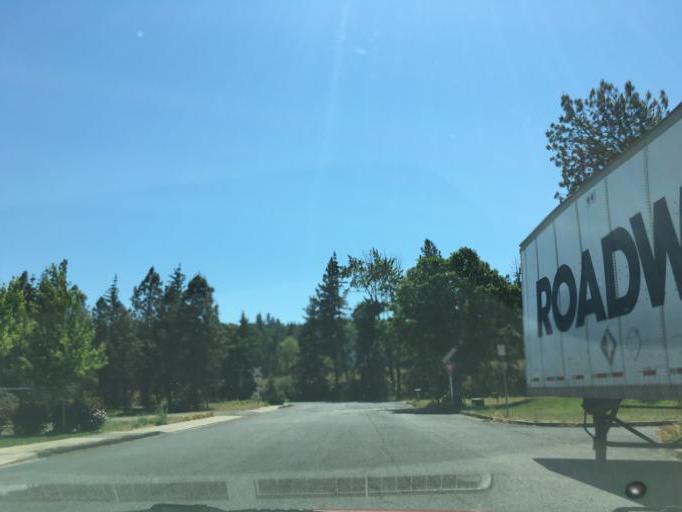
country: US
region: Oregon
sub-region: Hood River County
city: Hood River
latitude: 45.7138
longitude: -121.5190
